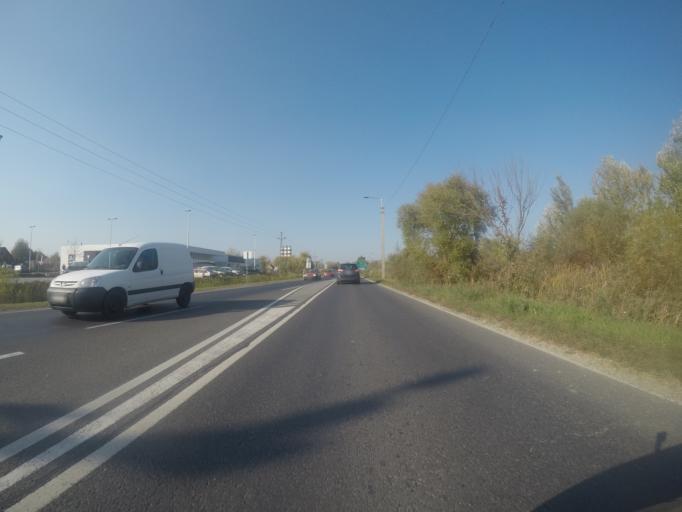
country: HU
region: Tolna
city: Dunafoldvar
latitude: 46.8095
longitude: 18.9120
